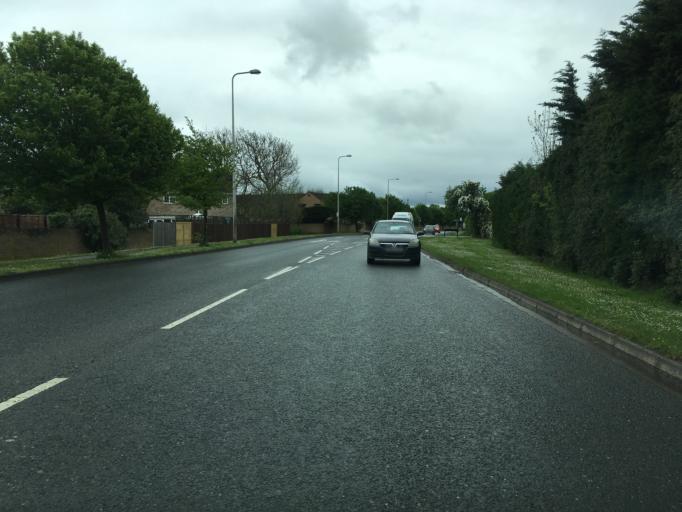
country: GB
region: England
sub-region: North Somerset
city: Kenn
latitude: 51.4300
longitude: -2.8467
